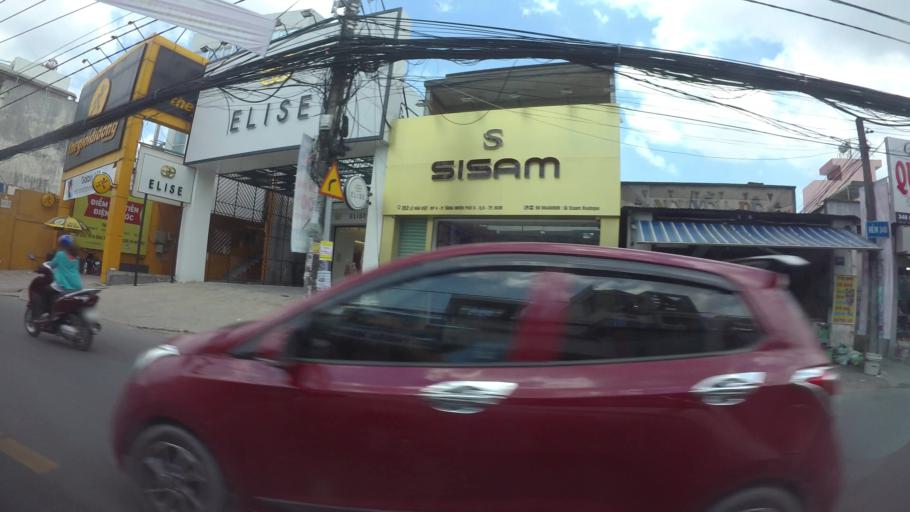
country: VN
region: Ho Chi Minh City
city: Thu Duc
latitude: 10.8441
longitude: 106.7837
